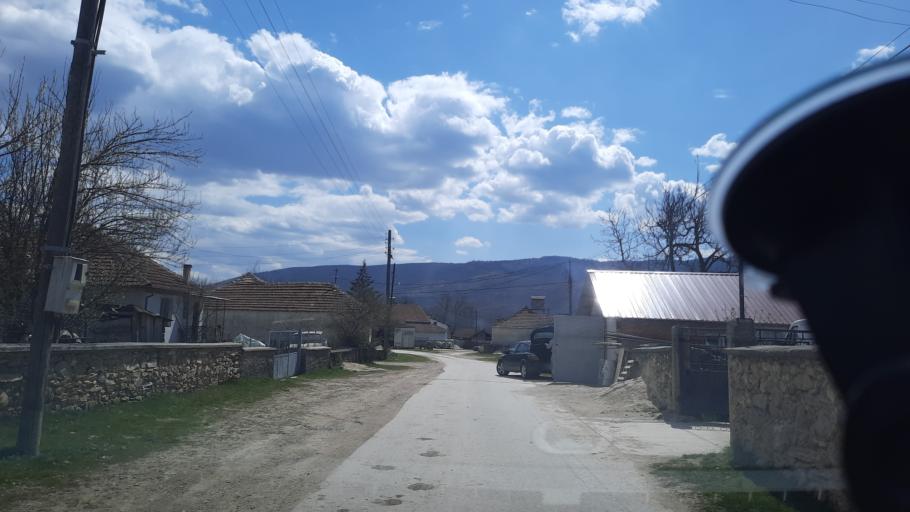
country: MK
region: Demir Hisar
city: Sopotnica
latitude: 41.2981
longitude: 21.1525
